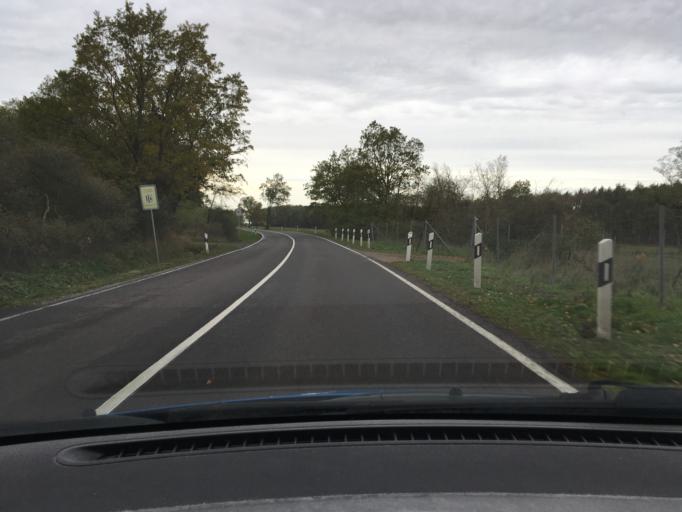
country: DE
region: Saxony-Anhalt
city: Leitzkau
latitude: 52.0329
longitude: 11.9928
